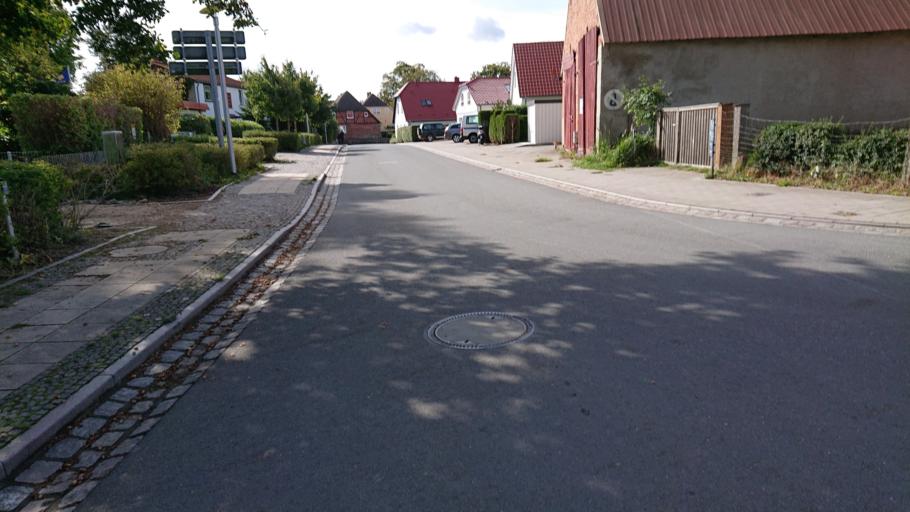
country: DE
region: Mecklenburg-Vorpommern
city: Altefahr
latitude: 54.3316
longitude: 13.1267
